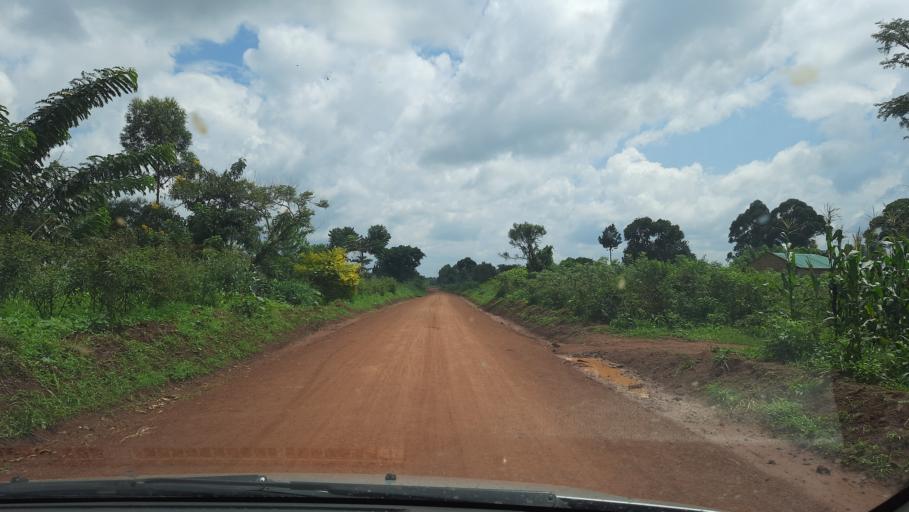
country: UG
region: Western Region
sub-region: Kiryandongo District
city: Kiryandongo
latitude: 1.8188
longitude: 31.9865
